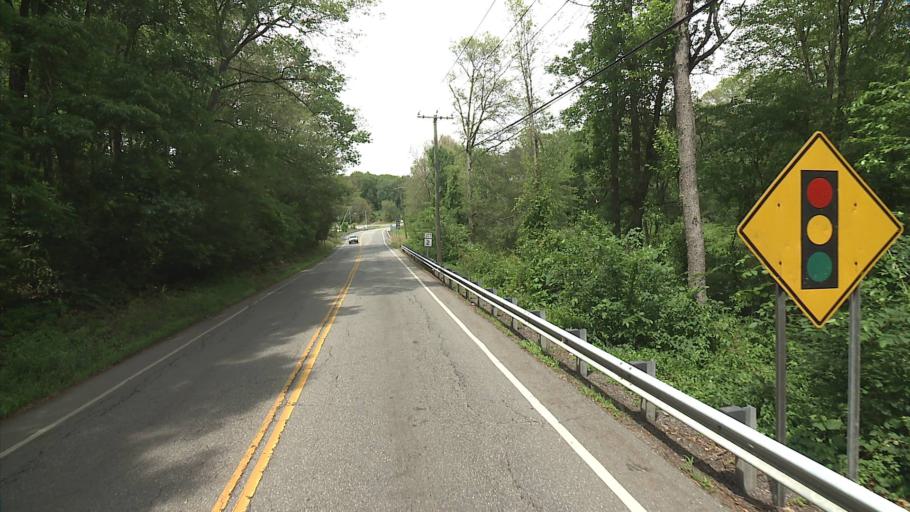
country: US
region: Connecticut
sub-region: New London County
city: Norwich
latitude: 41.4970
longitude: -72.0329
